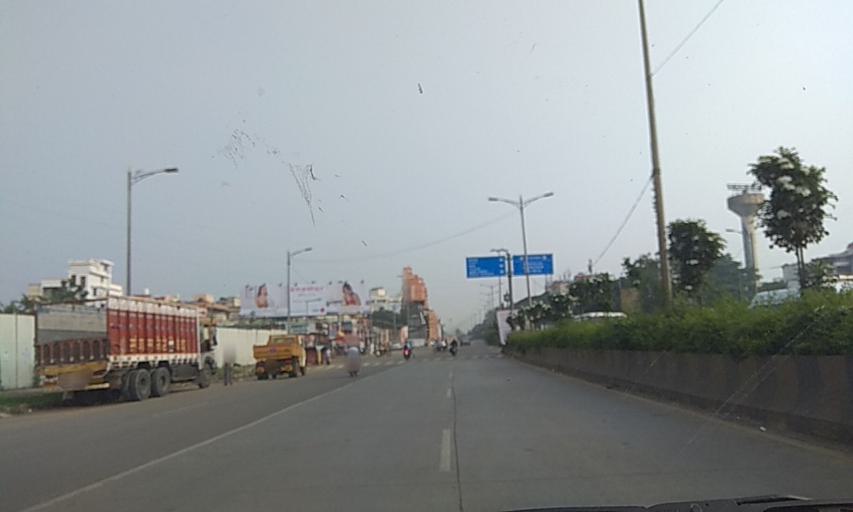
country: IN
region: Maharashtra
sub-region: Pune Division
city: Lohogaon
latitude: 18.5571
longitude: 73.9379
